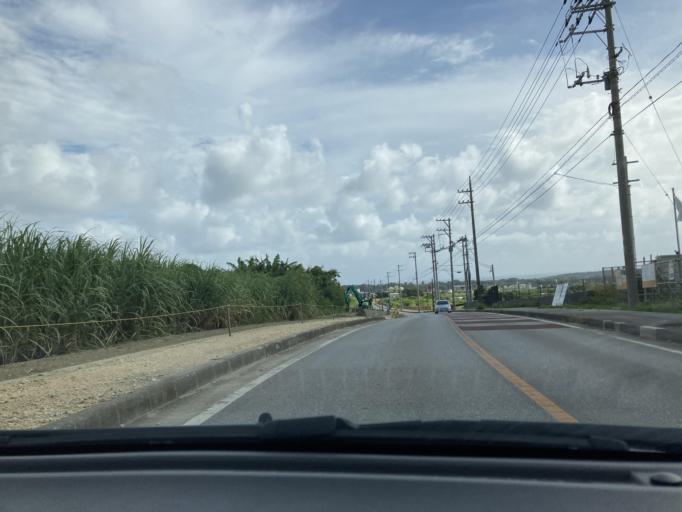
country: JP
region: Okinawa
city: Itoman
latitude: 26.1095
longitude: 127.6943
